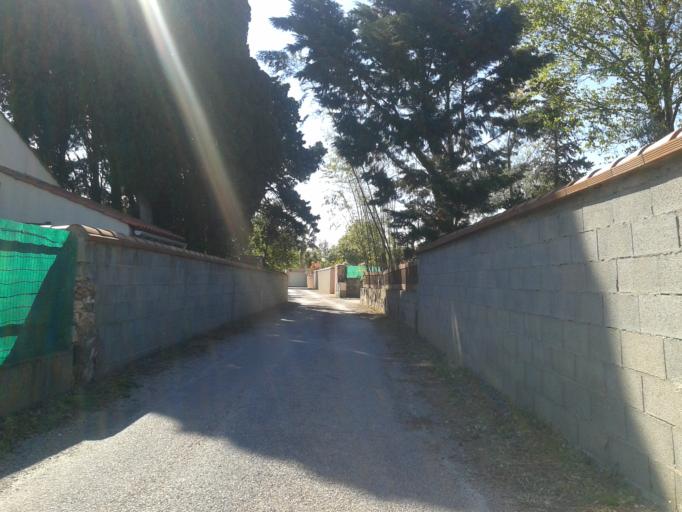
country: FR
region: Languedoc-Roussillon
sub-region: Departement des Pyrenees-Orientales
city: Pezilla-la-Riviere
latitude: 42.6979
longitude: 2.7689
